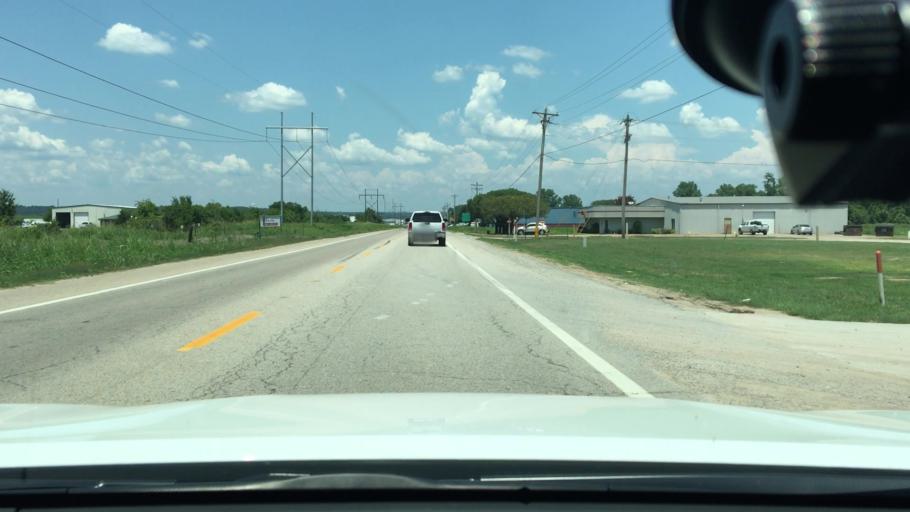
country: US
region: Arkansas
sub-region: Crawford County
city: Van Buren
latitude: 35.4065
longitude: -94.3300
